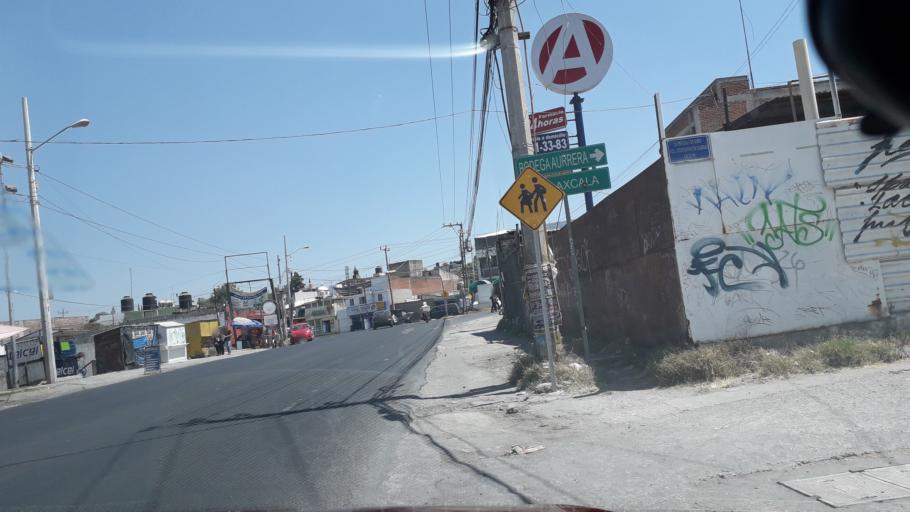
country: MX
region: Puebla
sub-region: Cuautlancingo
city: Sanctorum
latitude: 19.1001
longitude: -98.2290
